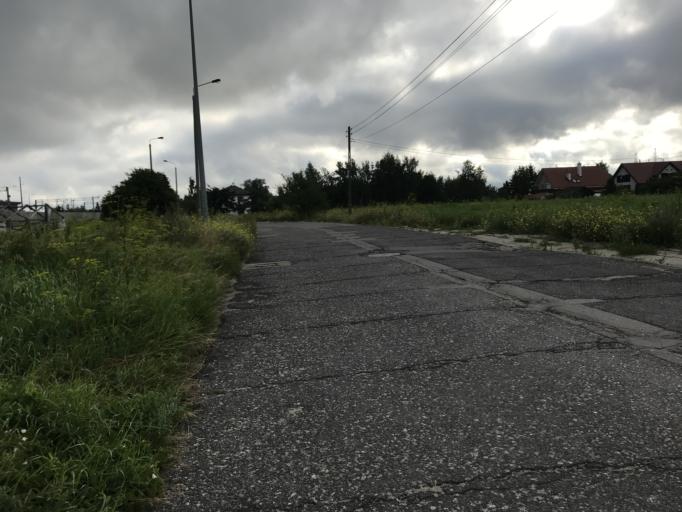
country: PL
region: Pomeranian Voivodeship
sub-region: Gdansk
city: Gdansk
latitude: 54.3370
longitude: 18.6800
